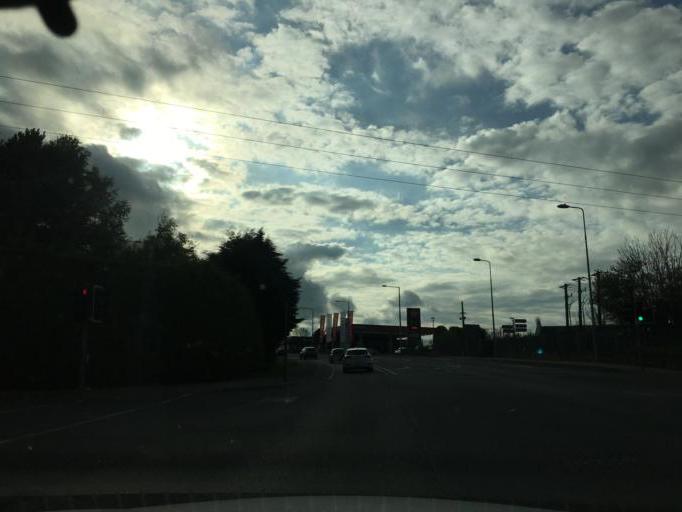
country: IE
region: Leinster
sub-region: Loch Garman
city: Loch Garman
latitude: 52.3421
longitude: -6.4848
